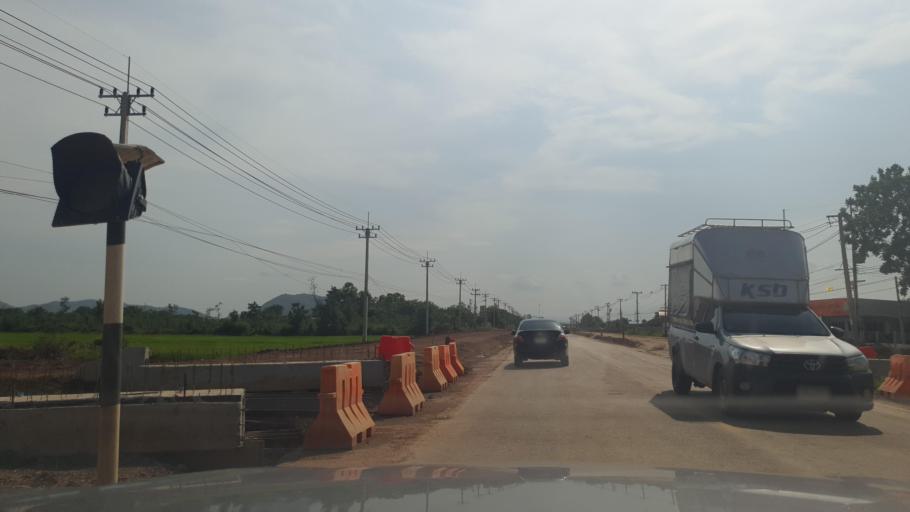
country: TH
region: Sukhothai
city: Sawankhalok
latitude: 17.3088
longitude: 99.7566
